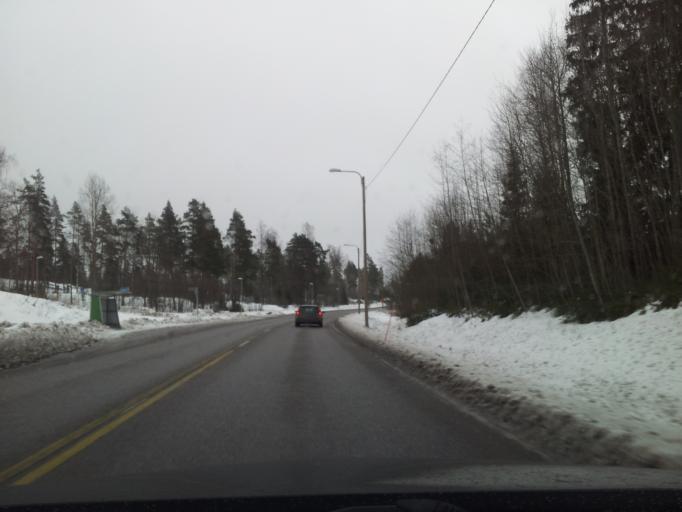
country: FI
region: Uusimaa
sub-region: Helsinki
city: Espoo
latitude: 60.1494
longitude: 24.5637
